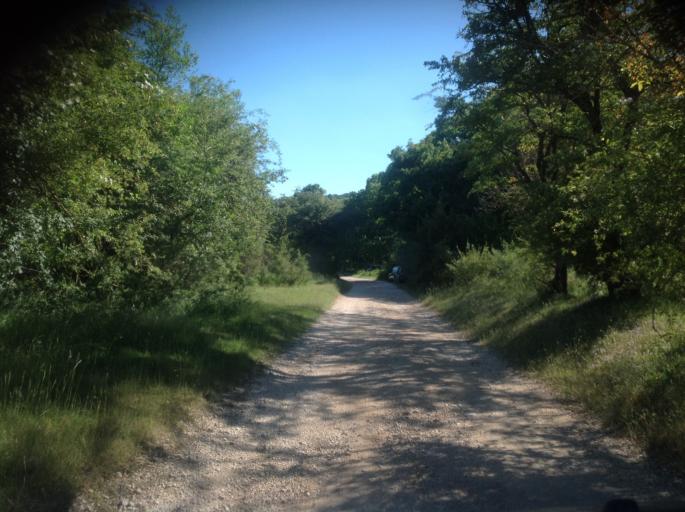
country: IT
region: Latium
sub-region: Provincia di Rieti
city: Limiti di Greccio
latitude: 42.4765
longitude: 12.7095
